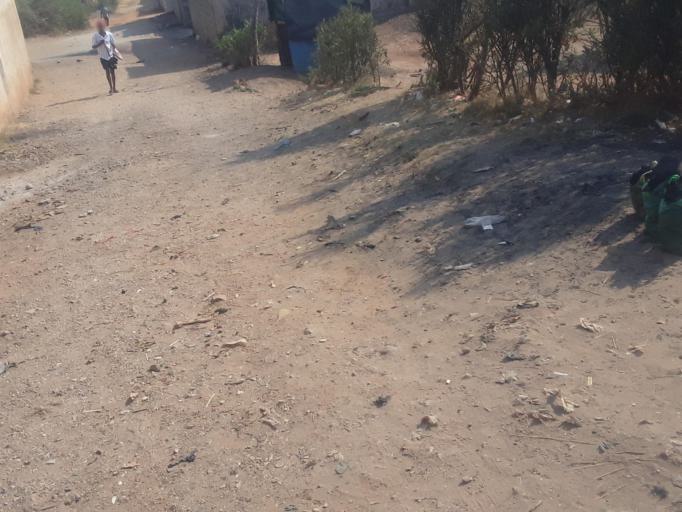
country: ZM
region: Lusaka
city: Lusaka
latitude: -15.3594
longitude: 28.3002
